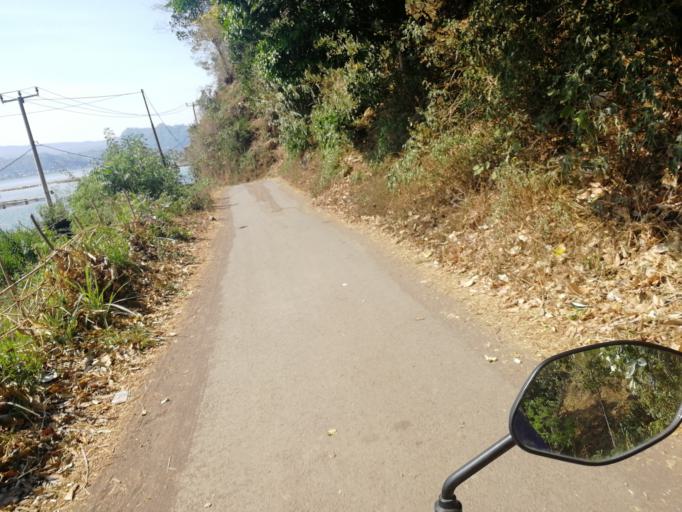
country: ID
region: Bali
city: Banjar Trunyan
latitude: -8.2626
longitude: 115.4226
